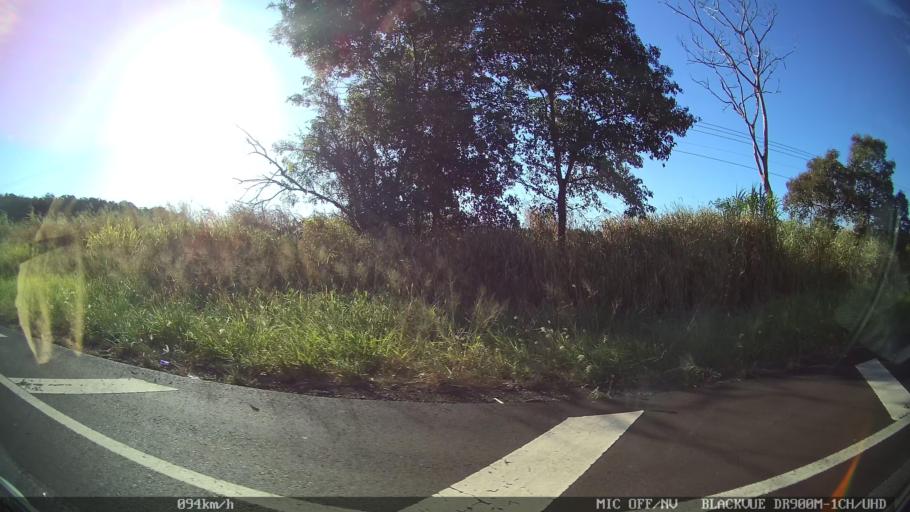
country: BR
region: Sao Paulo
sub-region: Olimpia
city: Olimpia
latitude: -20.7245
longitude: -49.0313
